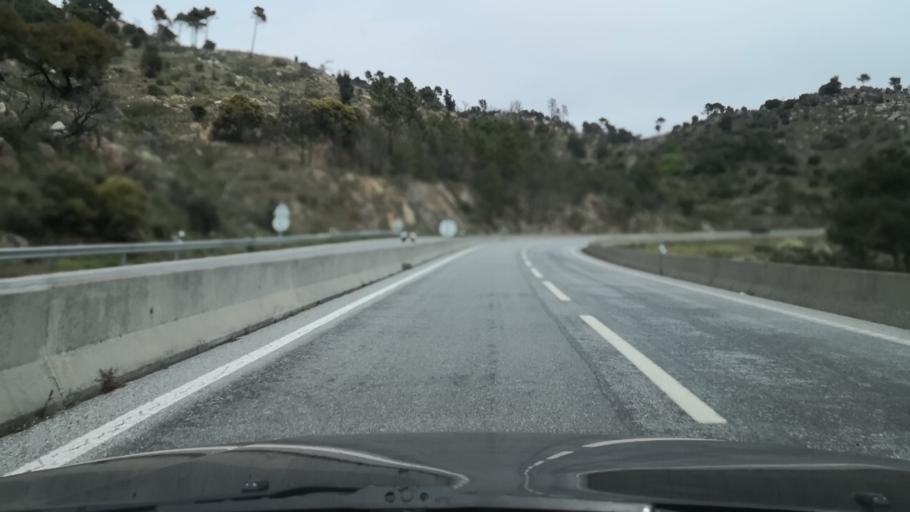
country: PT
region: Guarda
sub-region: Guarda
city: Guarda
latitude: 40.6018
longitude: -7.2778
